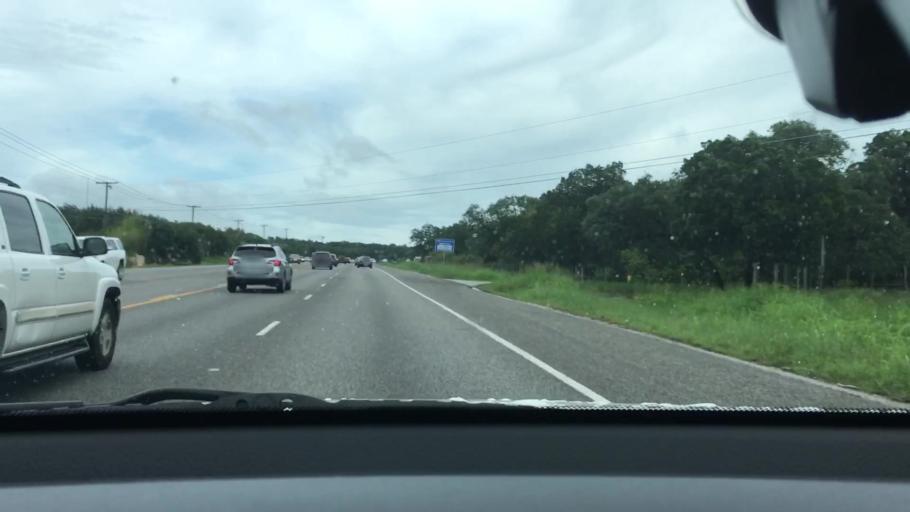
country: US
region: Texas
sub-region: Travis County
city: Bee Cave
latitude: 30.2931
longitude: -97.9224
